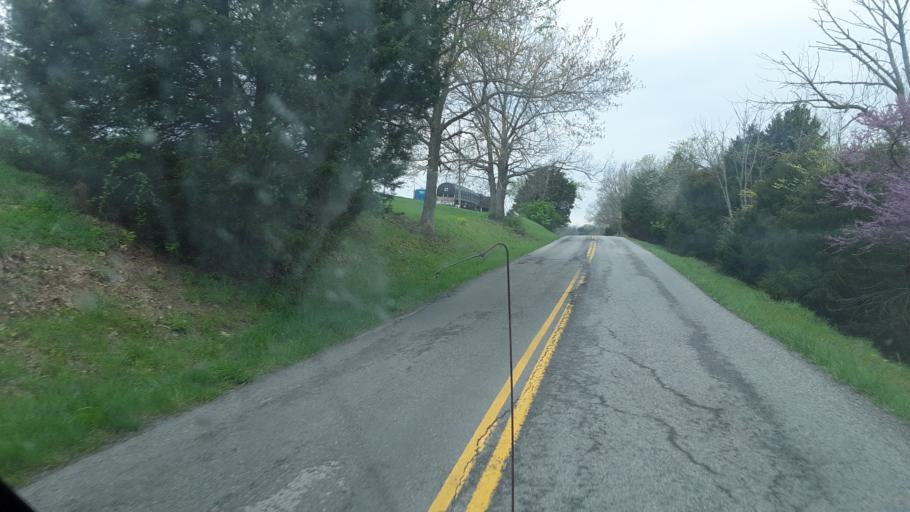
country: US
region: Kentucky
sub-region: Grant County
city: Dry Ridge
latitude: 38.6442
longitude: -84.7262
